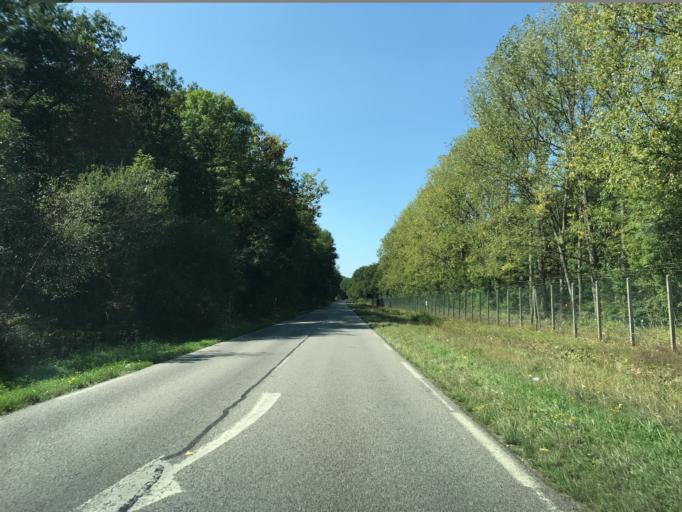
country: FR
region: Haute-Normandie
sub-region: Departement de l'Eure
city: La Chapelle-Reanville
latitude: 49.0941
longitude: 1.4061
